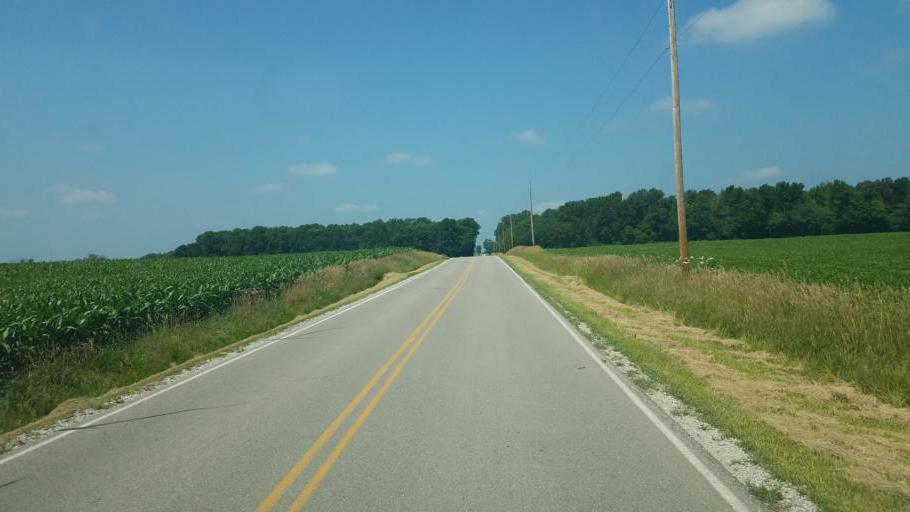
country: US
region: Ohio
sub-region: Crawford County
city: Bucyrus
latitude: 40.9937
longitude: -82.9281
